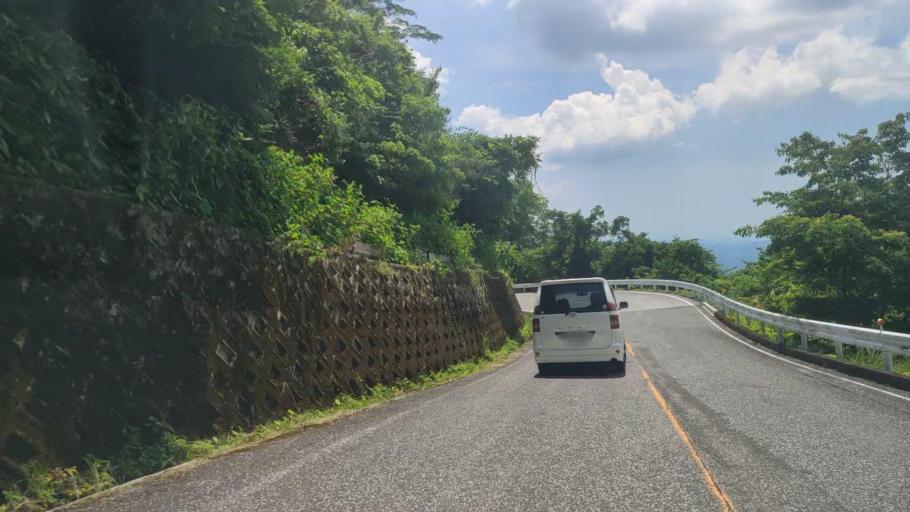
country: JP
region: Gifu
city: Tarui
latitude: 35.3865
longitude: 136.4418
